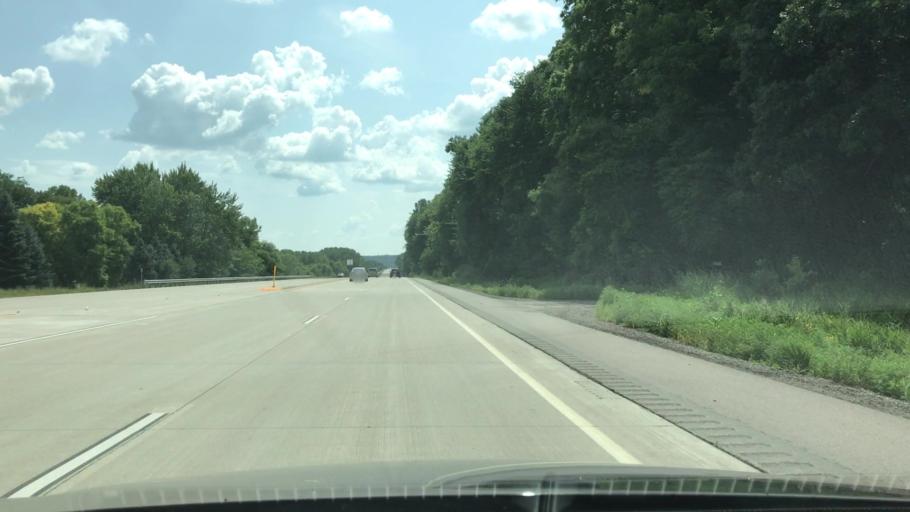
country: US
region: Minnesota
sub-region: Nicollet County
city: Saint Peter
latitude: 44.2890
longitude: -94.0009
